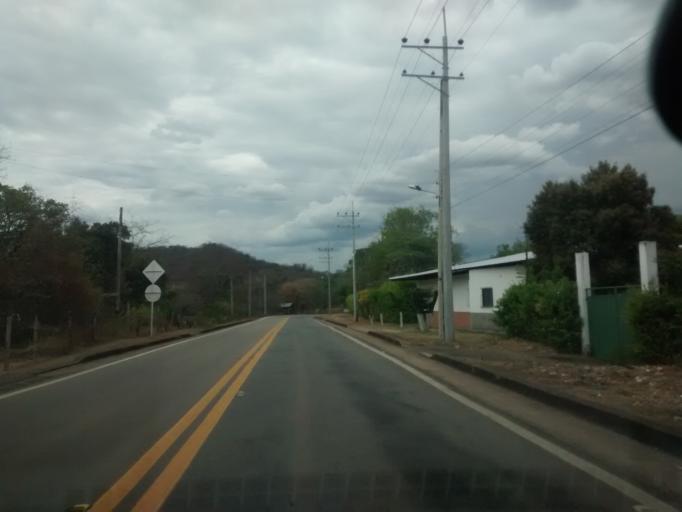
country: CO
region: Cundinamarca
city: Agua de Dios
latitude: 4.4299
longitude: -74.6908
